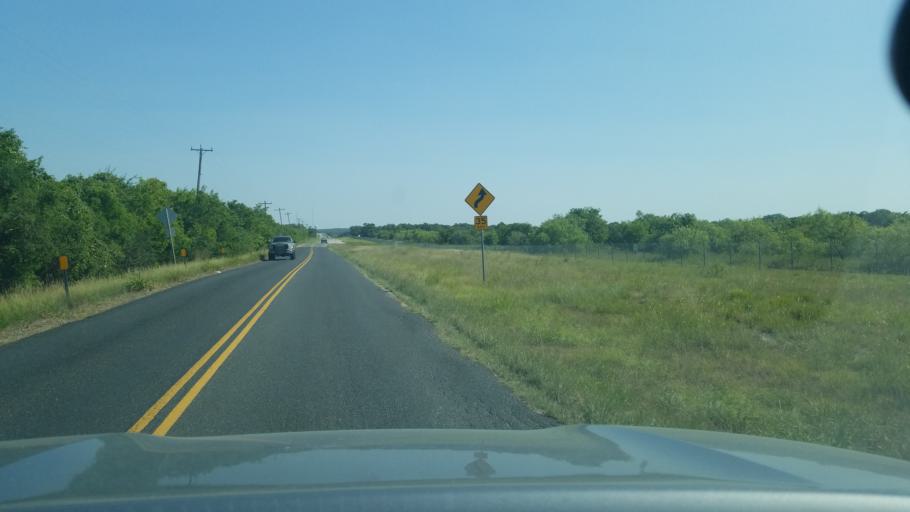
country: US
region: Texas
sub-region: Bexar County
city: Timberwood Park
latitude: 29.7394
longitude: -98.5129
